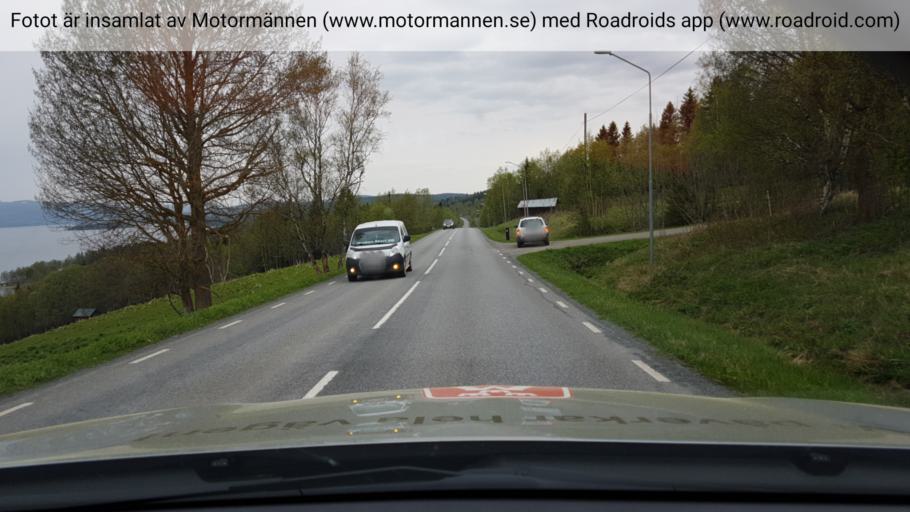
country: SE
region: Jaemtland
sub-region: Are Kommun
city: Jarpen
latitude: 63.4510
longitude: 13.3744
